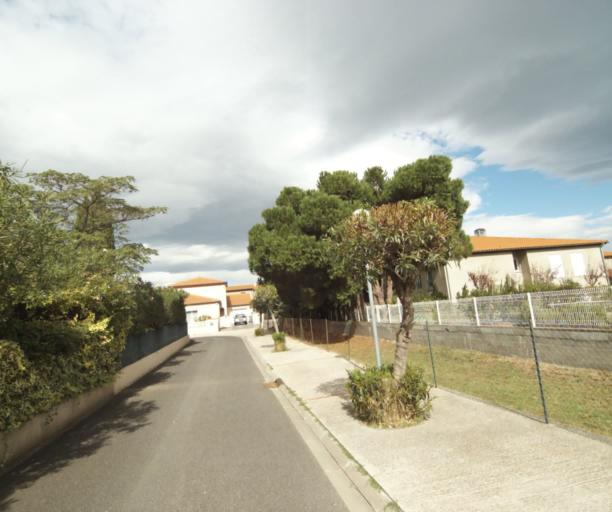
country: FR
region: Languedoc-Roussillon
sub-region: Departement des Pyrenees-Orientales
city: Argelers
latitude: 42.5545
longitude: 3.0236
